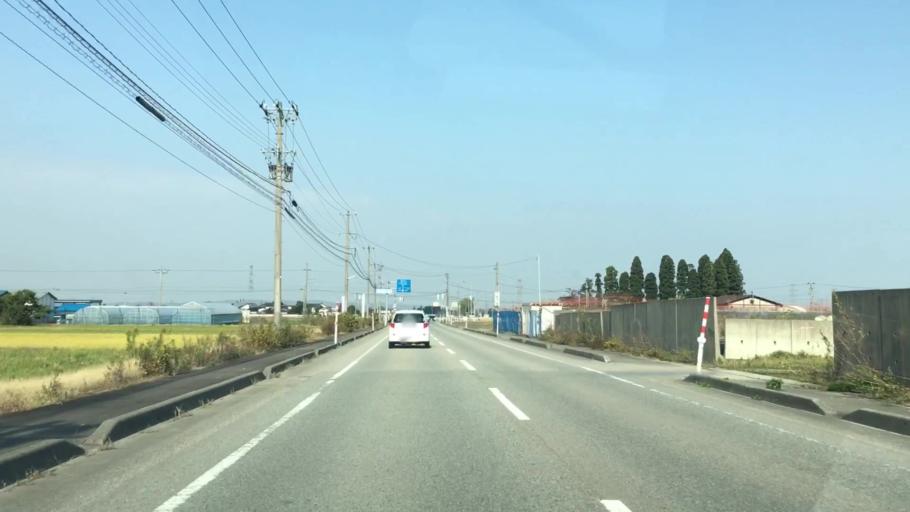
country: JP
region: Toyama
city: Yatsuomachi-higashikumisaka
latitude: 36.6108
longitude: 137.1922
